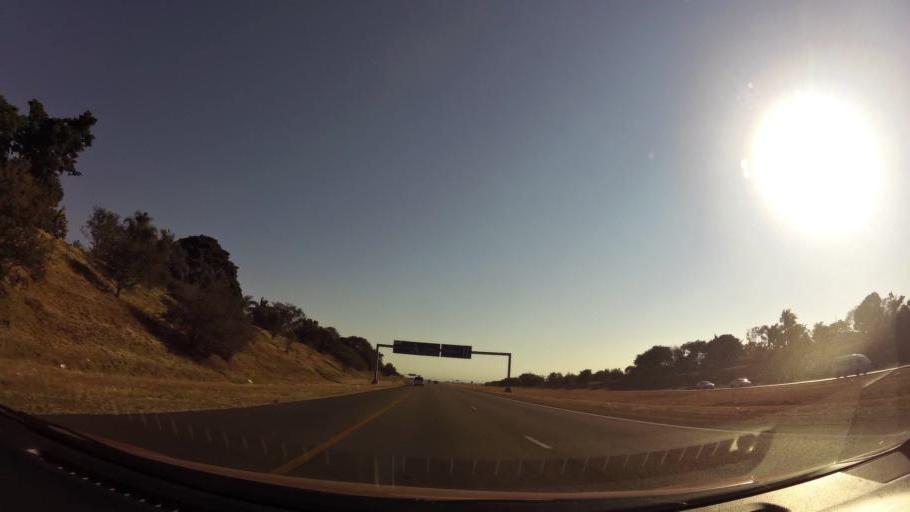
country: ZA
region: Gauteng
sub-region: City of Tshwane Metropolitan Municipality
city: Pretoria
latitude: -25.6648
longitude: 28.1150
